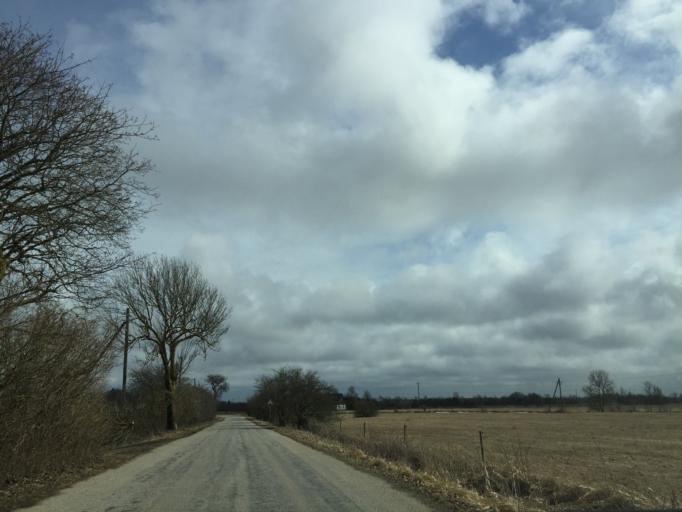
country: EE
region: Laeaene
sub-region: Lihula vald
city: Lihula
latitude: 58.7349
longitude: 23.8462
